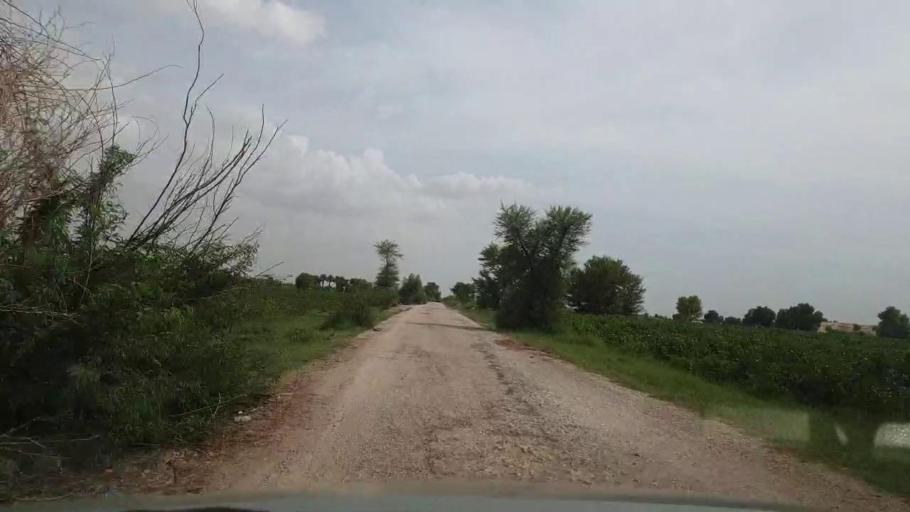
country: PK
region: Sindh
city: Kot Diji
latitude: 27.1341
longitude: 69.0280
